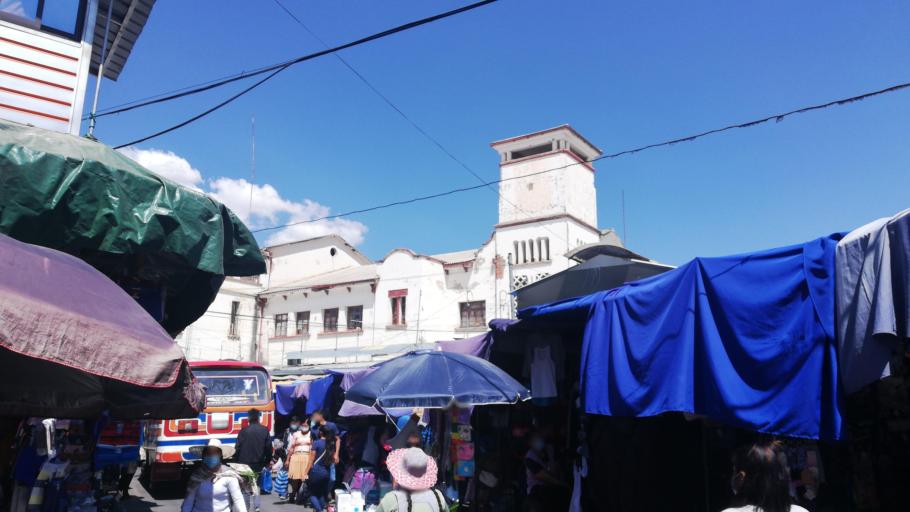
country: BO
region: Cochabamba
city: Cochabamba
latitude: -17.4031
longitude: -66.1544
